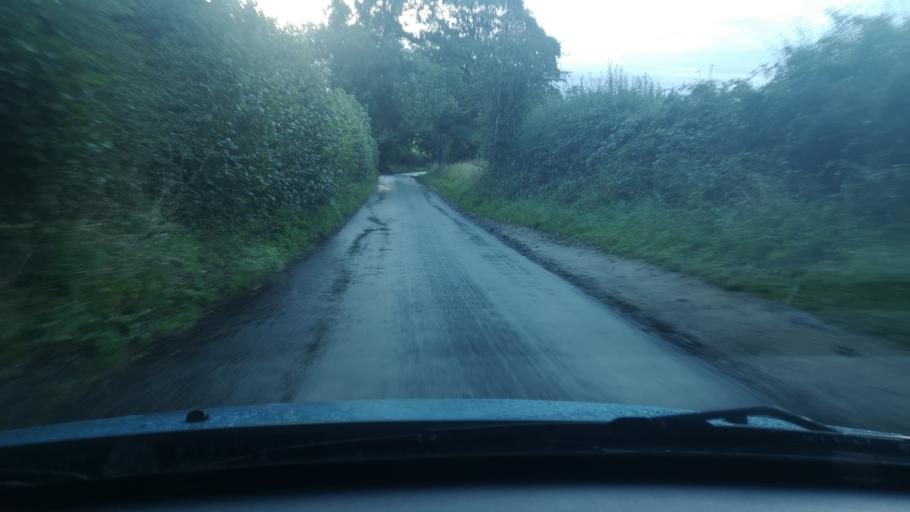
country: GB
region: England
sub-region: City and Borough of Wakefield
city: Low Ackworth
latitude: 53.6588
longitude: -1.3211
